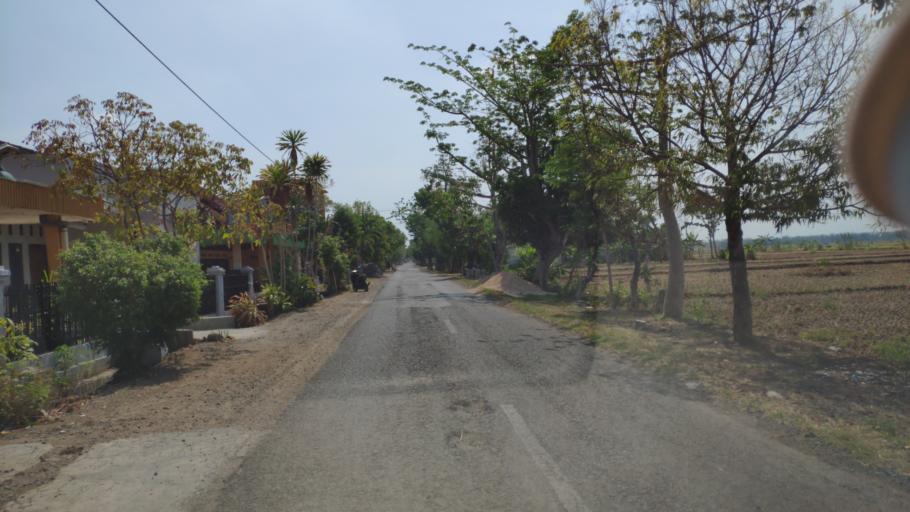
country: ID
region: Central Java
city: Kedungjenar
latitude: -6.9798
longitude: 111.4223
